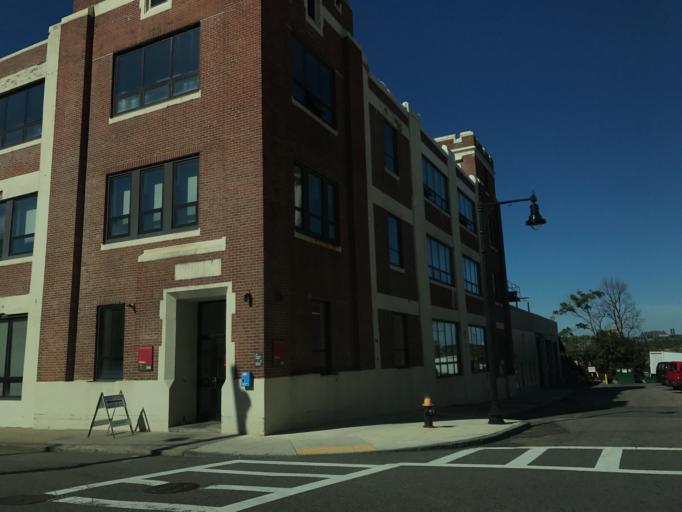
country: US
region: Massachusetts
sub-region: Norfolk County
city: Brookline
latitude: 42.3537
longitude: -71.1208
